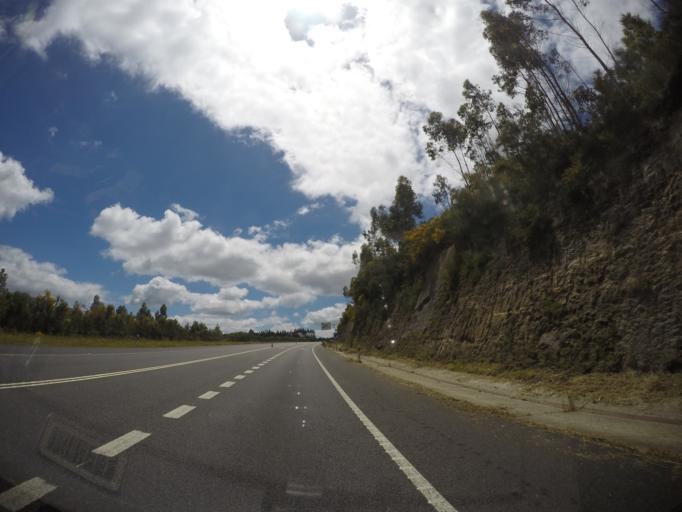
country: ES
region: Aragon
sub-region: Provincia de Zaragoza
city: Fuentes de Ebro
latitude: 41.5004
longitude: -0.6672
